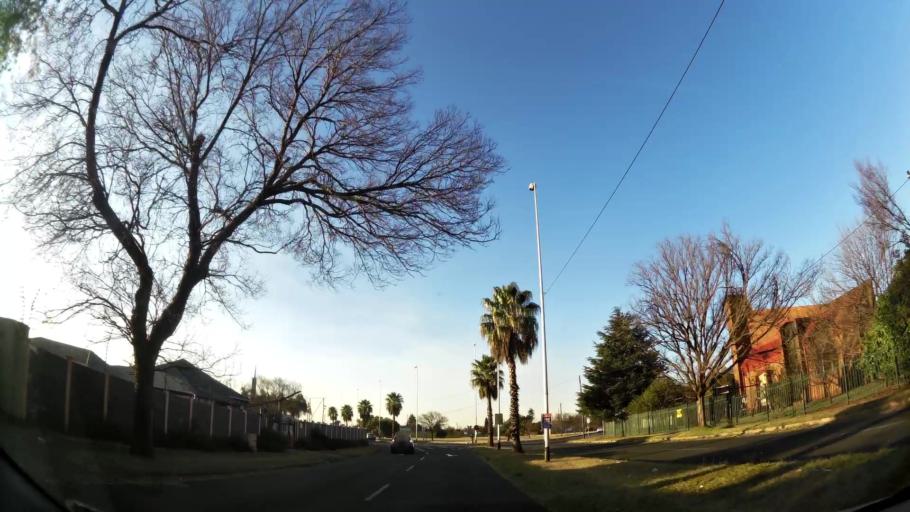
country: ZA
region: Gauteng
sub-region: City of Johannesburg Metropolitan Municipality
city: Roodepoort
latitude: -26.1528
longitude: 27.8781
